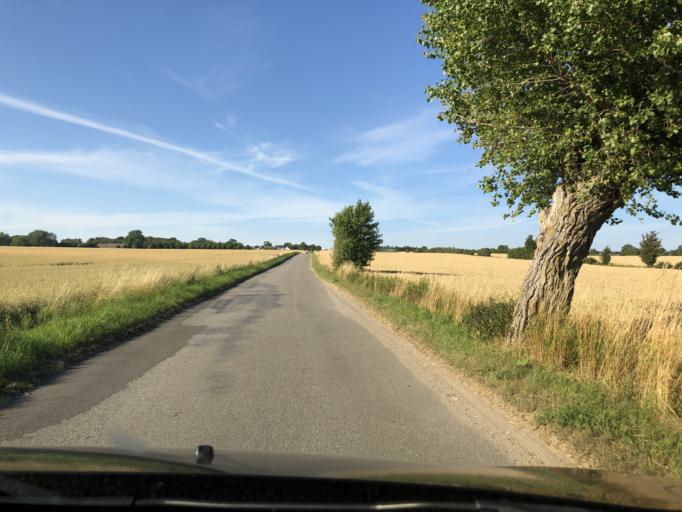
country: DK
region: South Denmark
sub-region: AEro Kommune
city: AEroskobing
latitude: 54.8584
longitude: 10.3647
